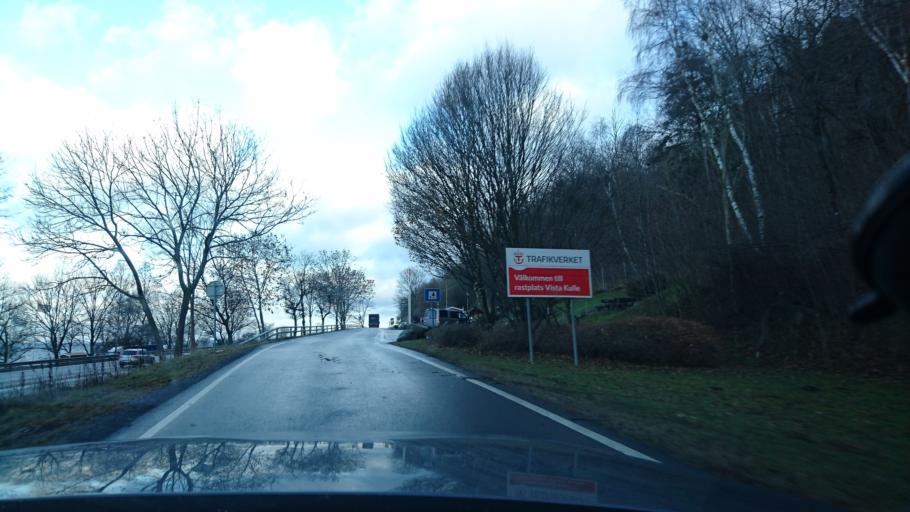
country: SE
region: Joenkoeping
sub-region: Jonkopings Kommun
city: Kaxholmen
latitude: 57.8518
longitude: 14.2669
